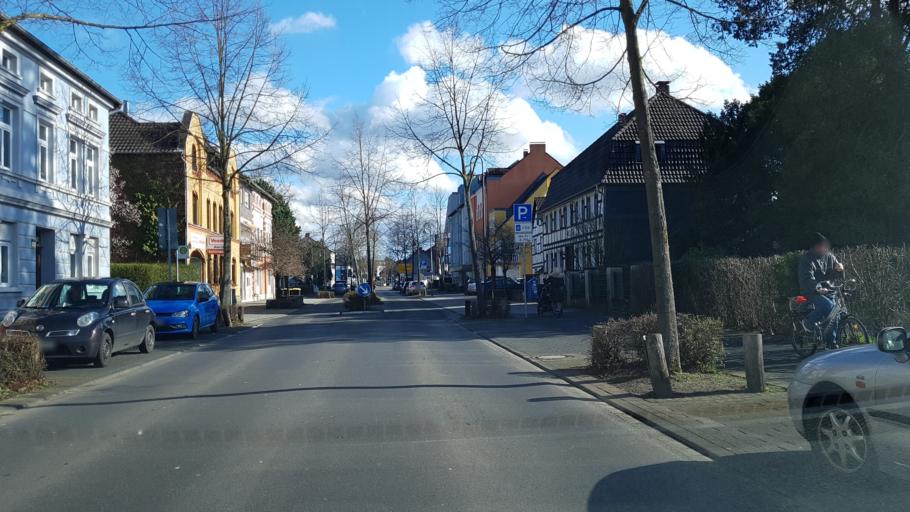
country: DE
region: North Rhine-Westphalia
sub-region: Regierungsbezirk Koln
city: Hennef
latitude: 50.7719
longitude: 7.2929
